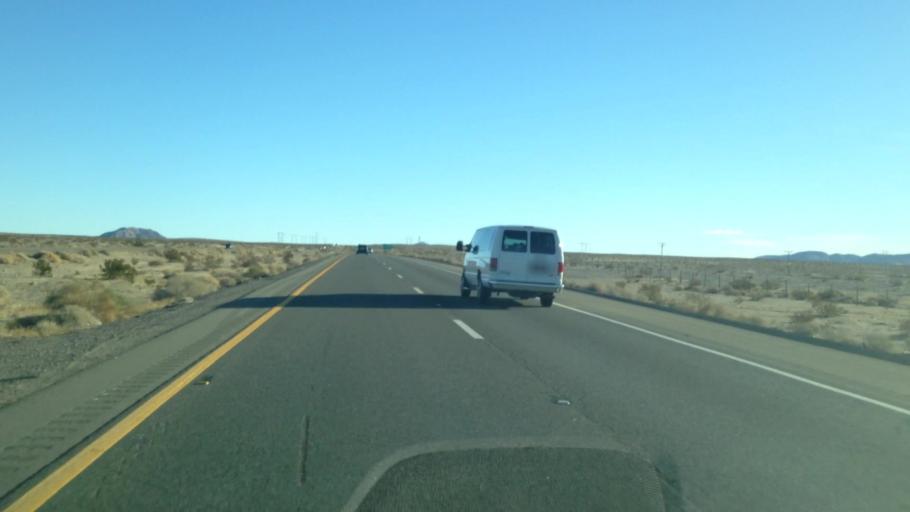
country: US
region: California
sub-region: San Bernardino County
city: Fort Irwin
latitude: 35.0018
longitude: -116.5564
